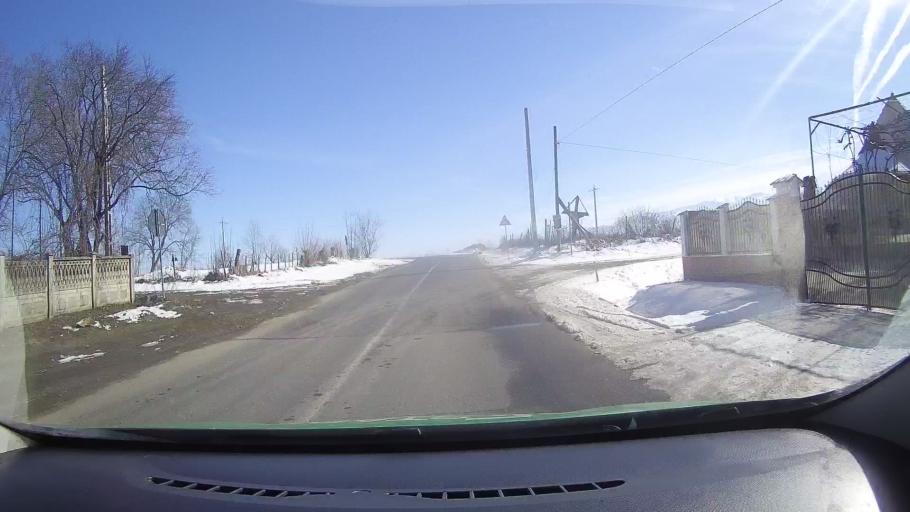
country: RO
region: Brasov
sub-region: Comuna Lisa
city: Lisa
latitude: 45.7239
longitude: 24.8545
